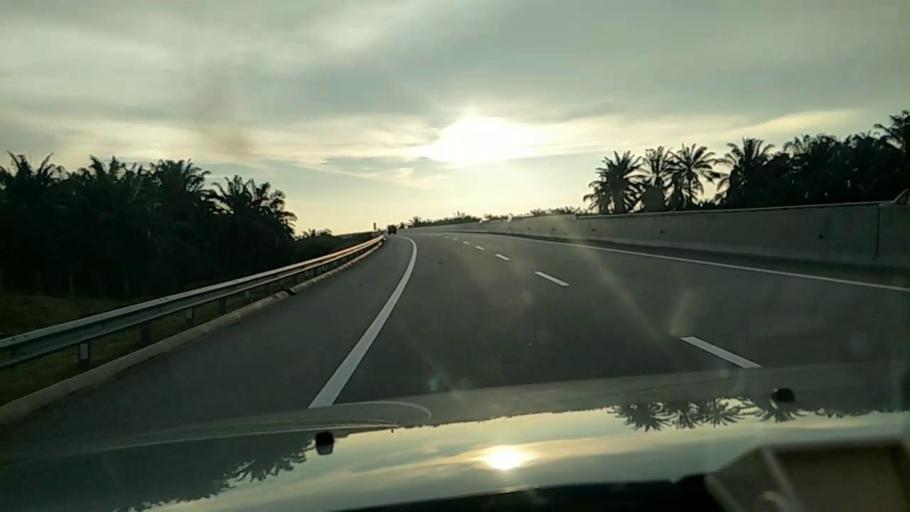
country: MY
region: Selangor
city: Batu Arang
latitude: 3.2883
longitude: 101.4348
